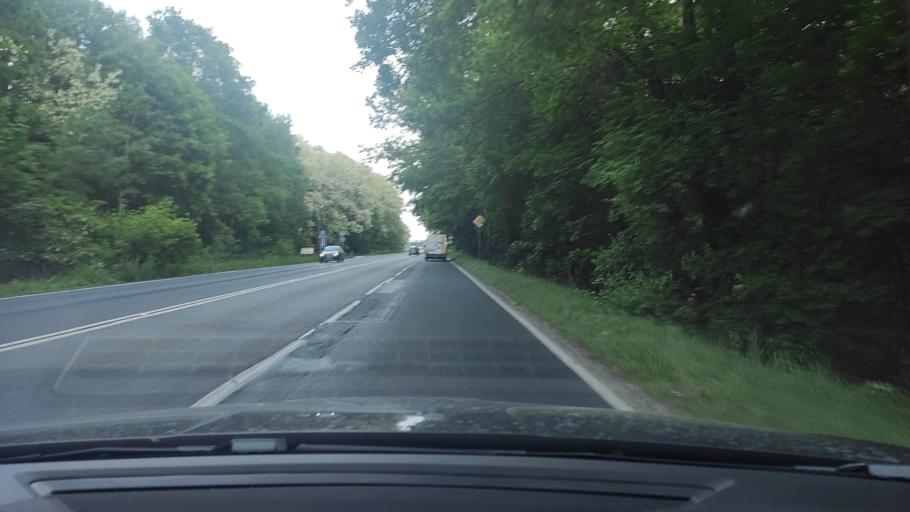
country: PL
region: Greater Poland Voivodeship
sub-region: Powiat poznanski
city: Czerwonak
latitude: 52.4196
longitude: 17.0190
